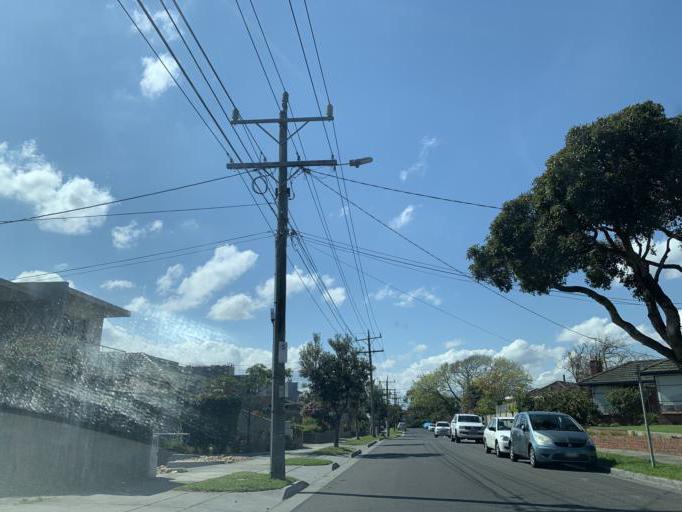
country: AU
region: Victoria
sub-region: Kingston
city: Mordialloc
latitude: -37.9985
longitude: 145.0797
